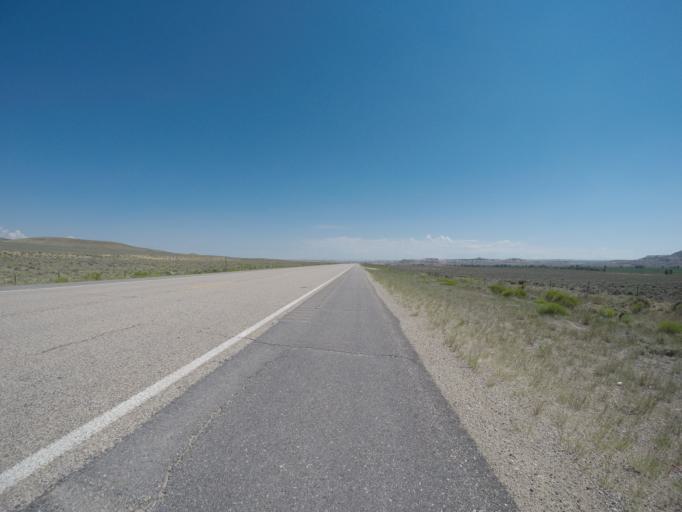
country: US
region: Wyoming
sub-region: Sublette County
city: Marbleton
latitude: 42.4417
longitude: -110.0965
